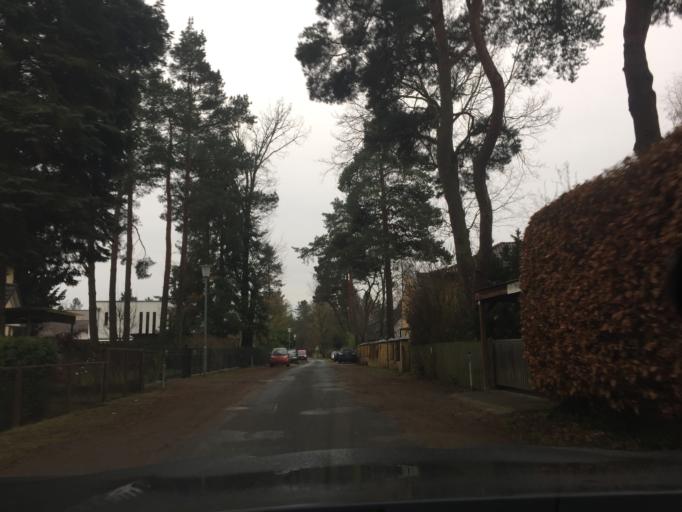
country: DE
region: Berlin
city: Kladow
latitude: 52.4601
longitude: 13.1030
